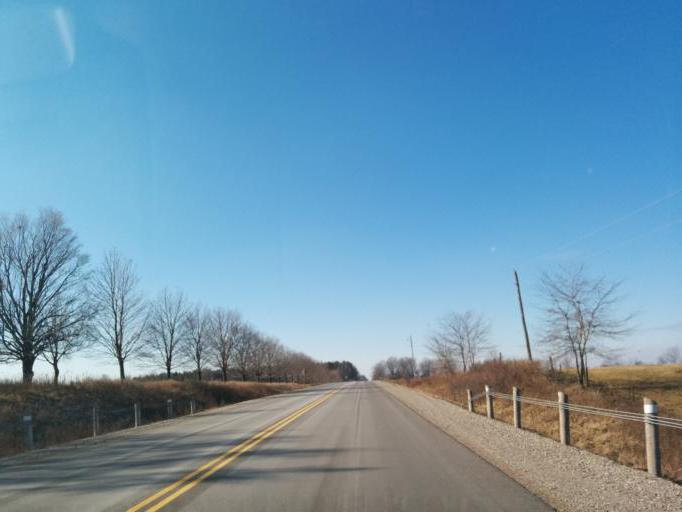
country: CA
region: Ontario
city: Brantford
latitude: 43.0381
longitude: -80.2898
